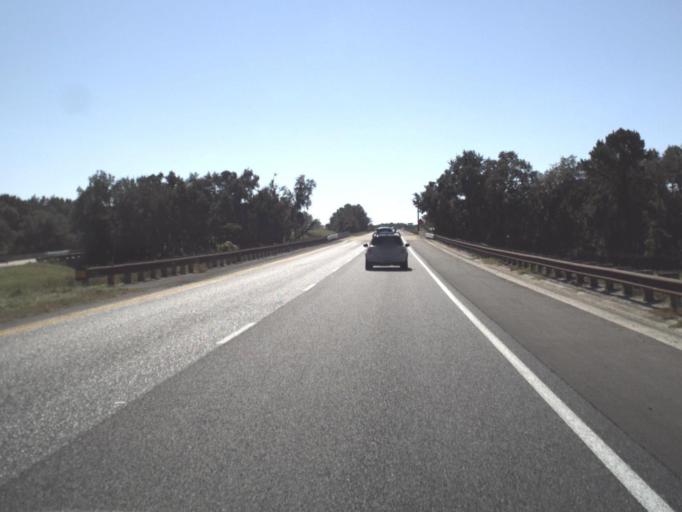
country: US
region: Florida
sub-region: Hernando County
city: Brookridge
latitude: 28.6186
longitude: -82.4937
